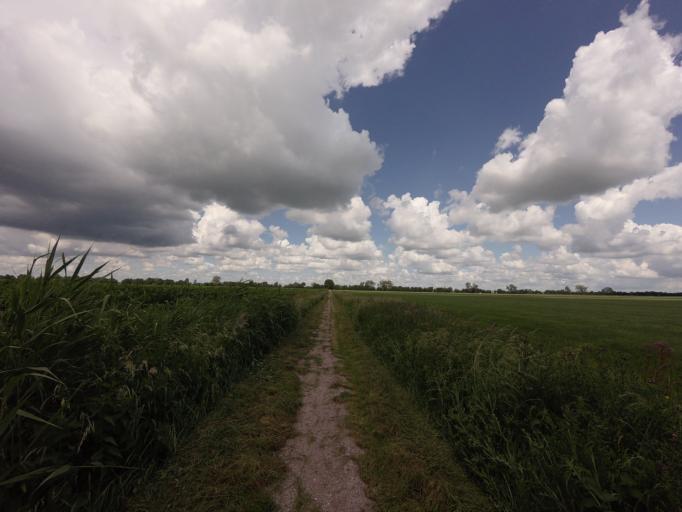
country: NL
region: South Holland
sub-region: Gemeente Schoonhoven
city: Schoonhoven
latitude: 51.9742
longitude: 4.8946
